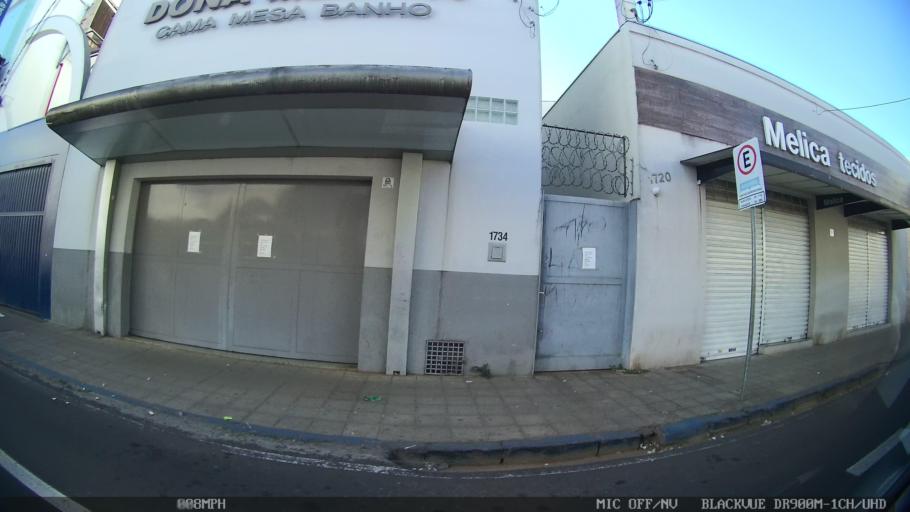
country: BR
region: Sao Paulo
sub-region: Franca
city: Franca
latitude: -20.5382
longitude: -47.4031
